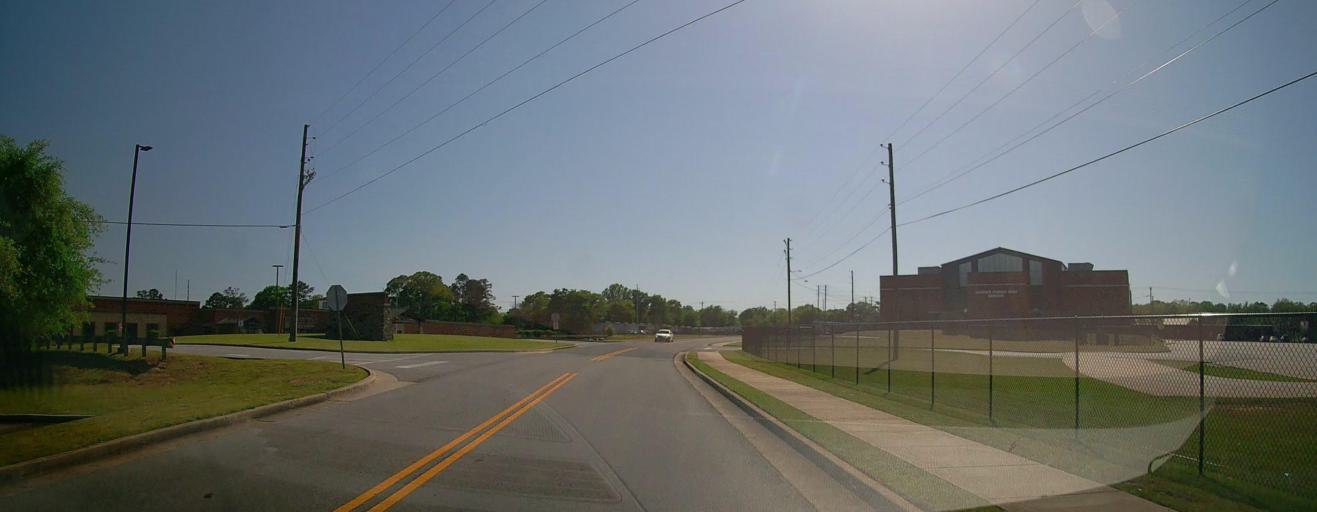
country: US
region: Georgia
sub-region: Houston County
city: Warner Robins
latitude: 32.6102
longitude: -83.6107
